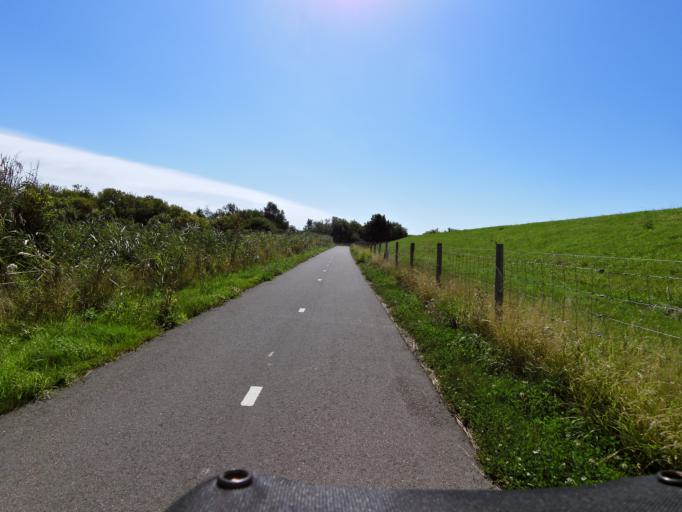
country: NL
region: South Holland
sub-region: Gemeente Goeree-Overflakkee
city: Goedereede
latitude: 51.8001
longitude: 4.0093
